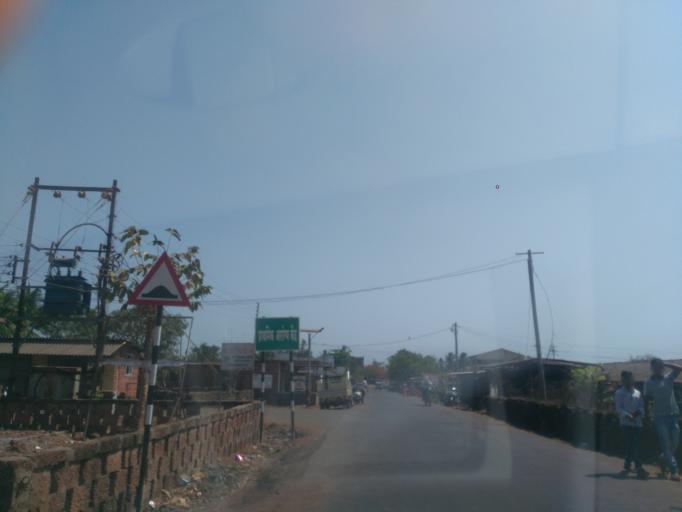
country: IN
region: Maharashtra
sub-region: Ratnagiri
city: Makhjan
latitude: 17.2374
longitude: 73.2701
